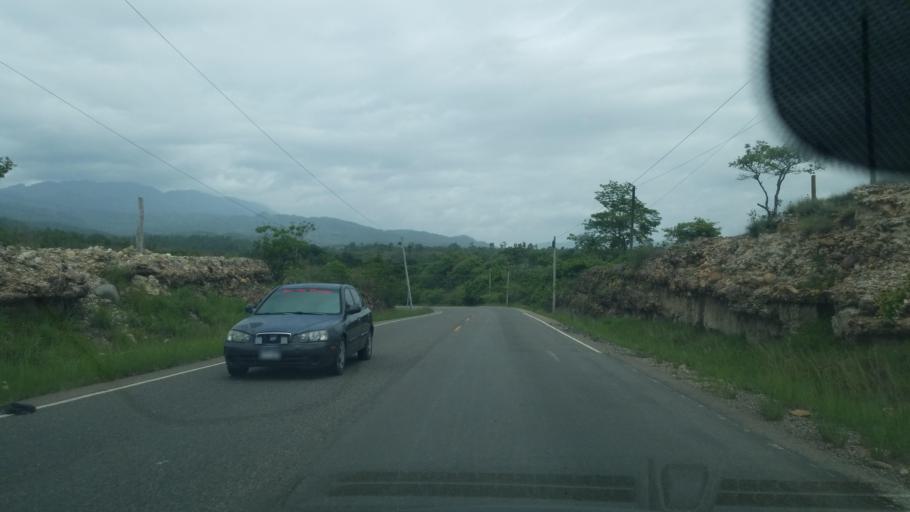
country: HN
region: Ocotepeque
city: Lucerna
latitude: 14.5248
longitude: -88.9506
